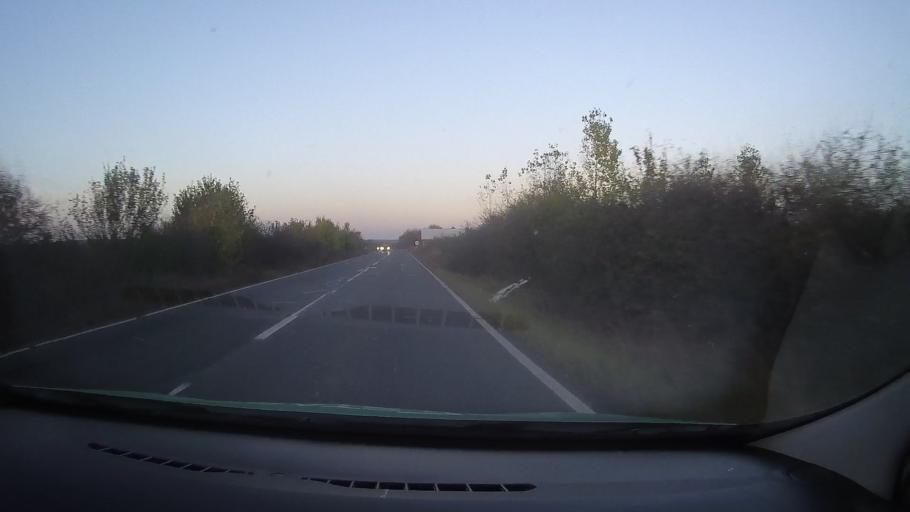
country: RO
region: Timis
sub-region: Comuna Dumbrava
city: Dumbrava
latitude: 45.8368
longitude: 22.1406
